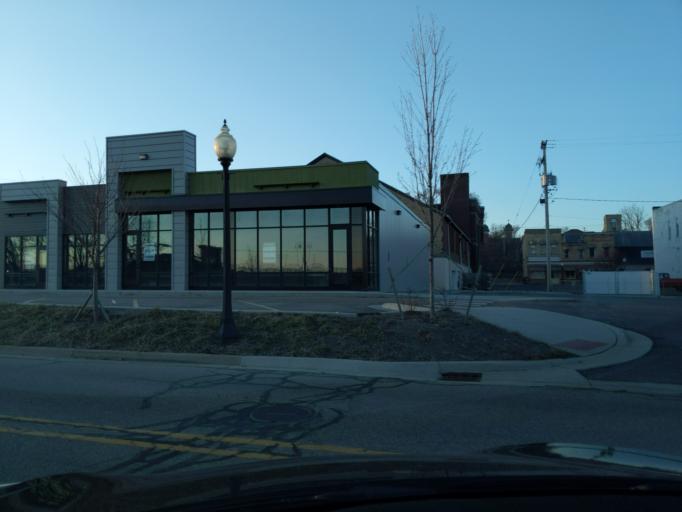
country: US
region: Michigan
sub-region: Ionia County
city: Ionia
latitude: 42.9813
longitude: -85.0694
